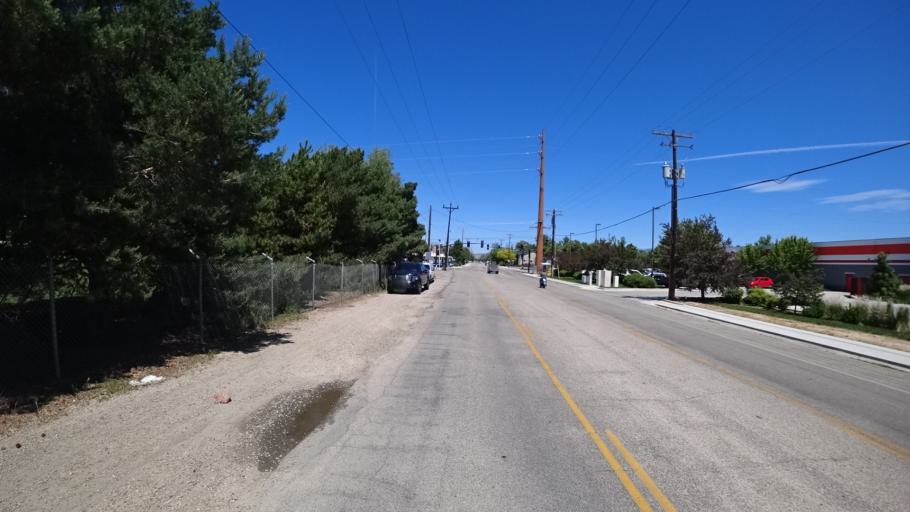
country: US
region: Idaho
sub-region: Ada County
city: Garden City
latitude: 43.5889
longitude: -116.2336
